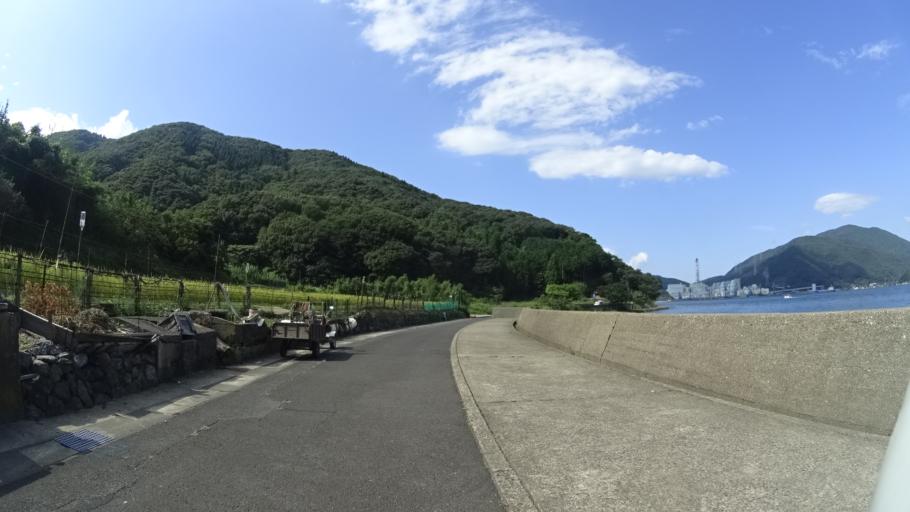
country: JP
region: Kyoto
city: Maizuru
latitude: 35.5098
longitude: 135.3315
